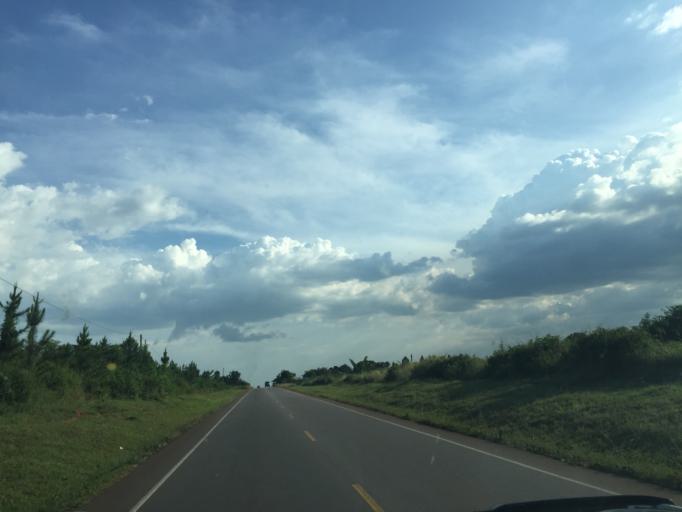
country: UG
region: Central Region
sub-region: Nakasongola District
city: Nakasongola
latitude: 1.1263
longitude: 32.4653
